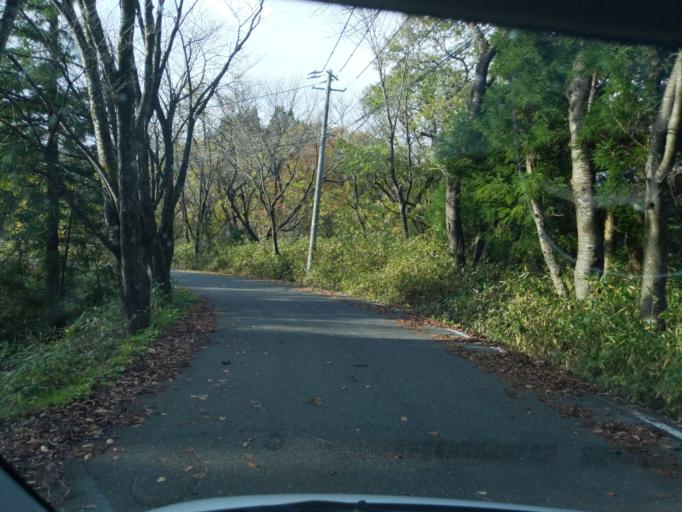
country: JP
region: Iwate
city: Ichinoseki
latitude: 39.0189
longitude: 141.1050
